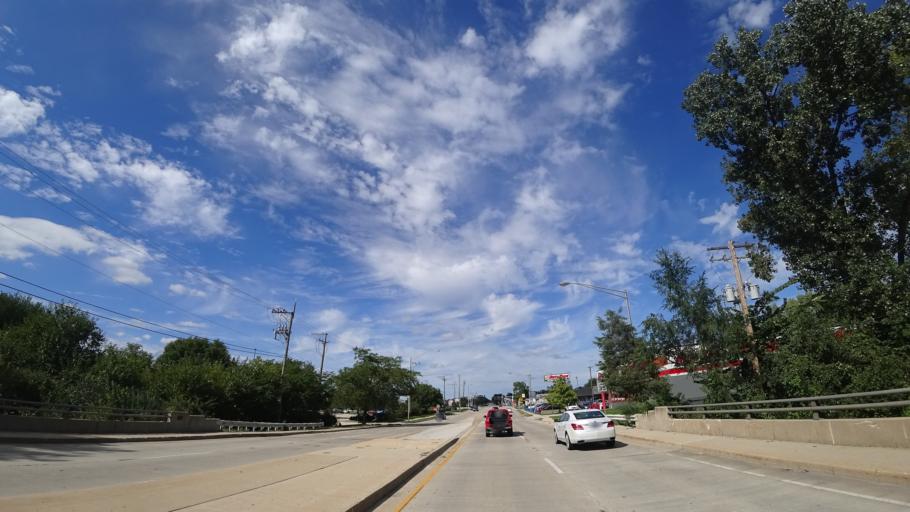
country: US
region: Illinois
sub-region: Cook County
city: Chicago Ridge
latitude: 41.7075
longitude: -87.7794
